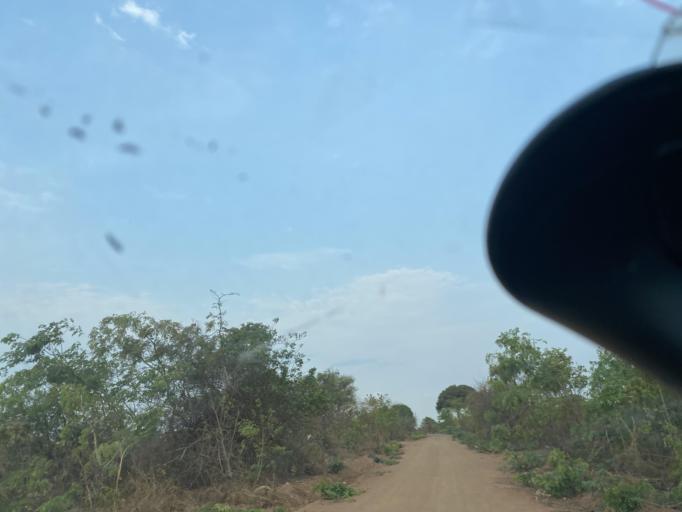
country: ZM
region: Lusaka
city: Chongwe
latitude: -15.2023
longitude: 28.5207
